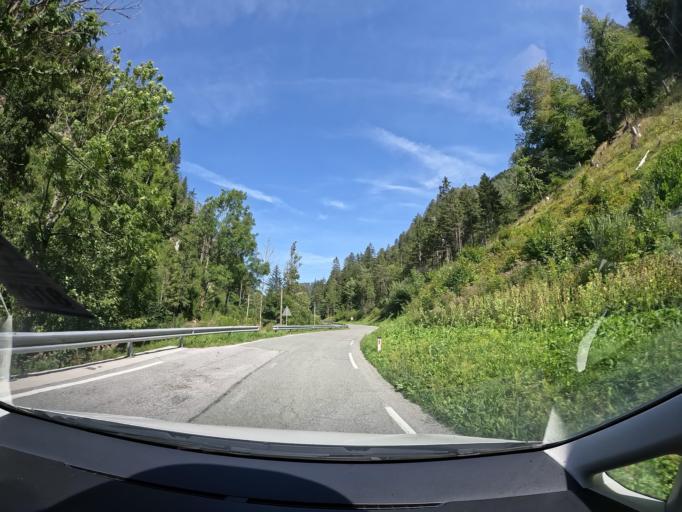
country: SI
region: Jesenice
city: Koroska Bela
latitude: 46.4758
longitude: 14.1044
